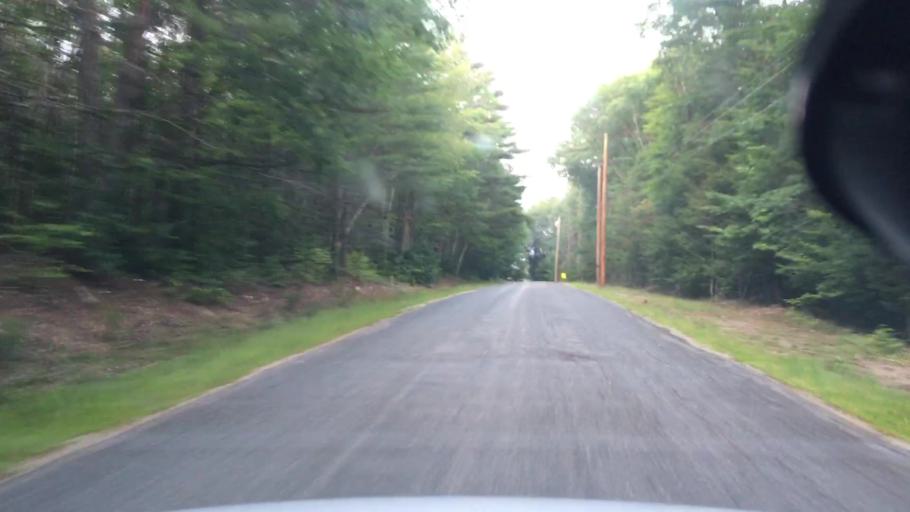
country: US
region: Maine
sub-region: Oxford County
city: Bethel
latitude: 44.4084
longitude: -70.8713
